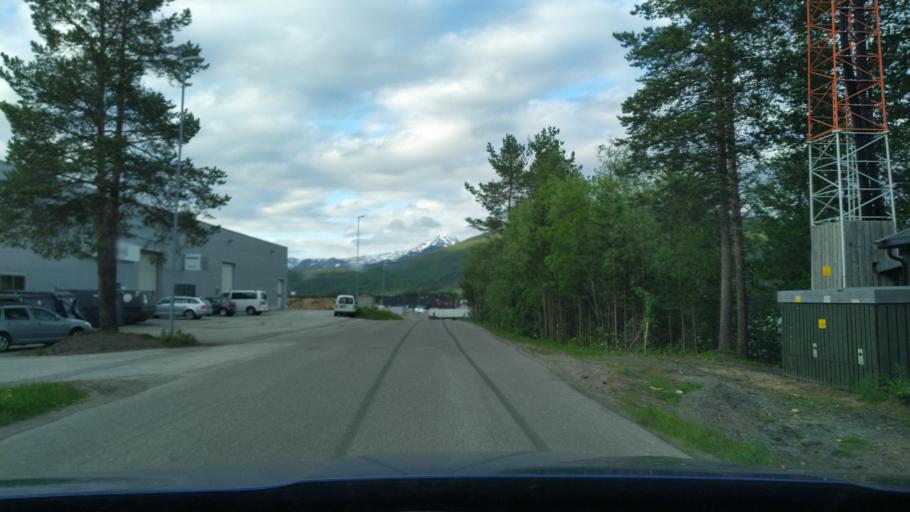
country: NO
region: Troms
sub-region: Malselv
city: Moen
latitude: 69.0914
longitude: 18.5886
